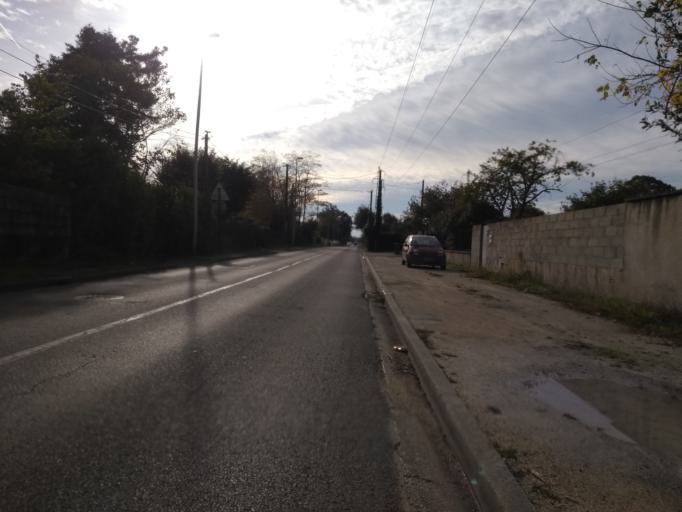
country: FR
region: Aquitaine
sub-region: Departement de la Gironde
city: Cestas
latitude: 44.7838
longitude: -0.6739
